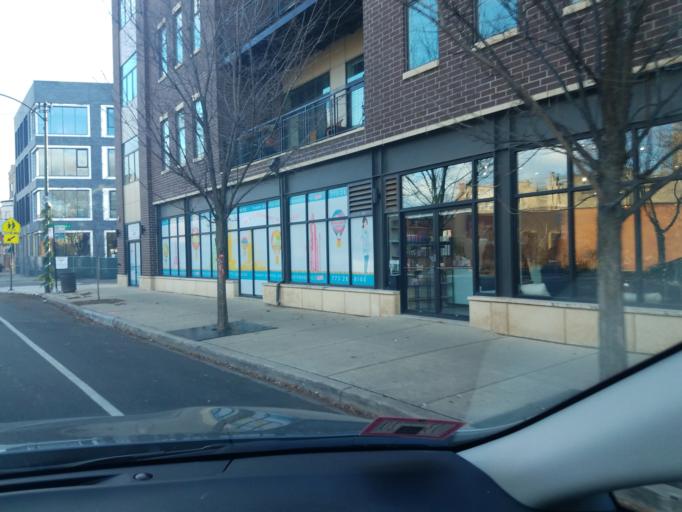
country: US
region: Illinois
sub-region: Cook County
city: Lincolnwood
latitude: 41.9455
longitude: -87.6728
